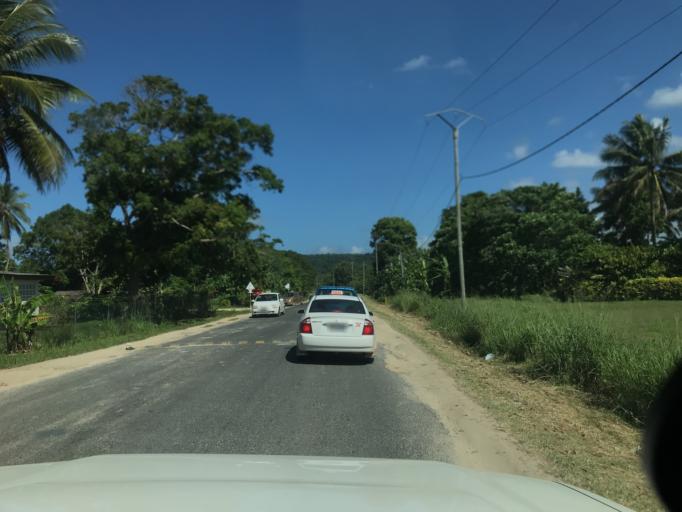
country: VU
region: Sanma
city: Luganville
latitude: -15.5183
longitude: 167.1667
